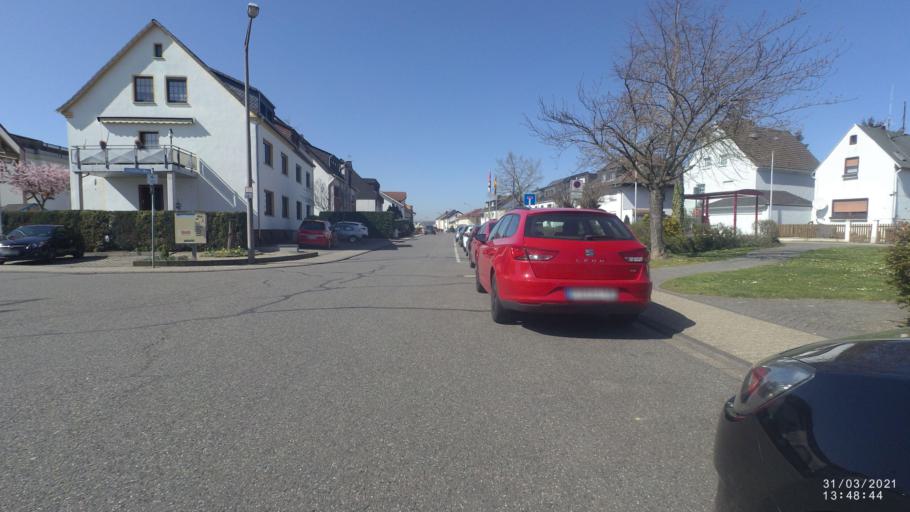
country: DE
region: Rheinland-Pfalz
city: Kaltenengers
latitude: 50.4124
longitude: 7.5572
